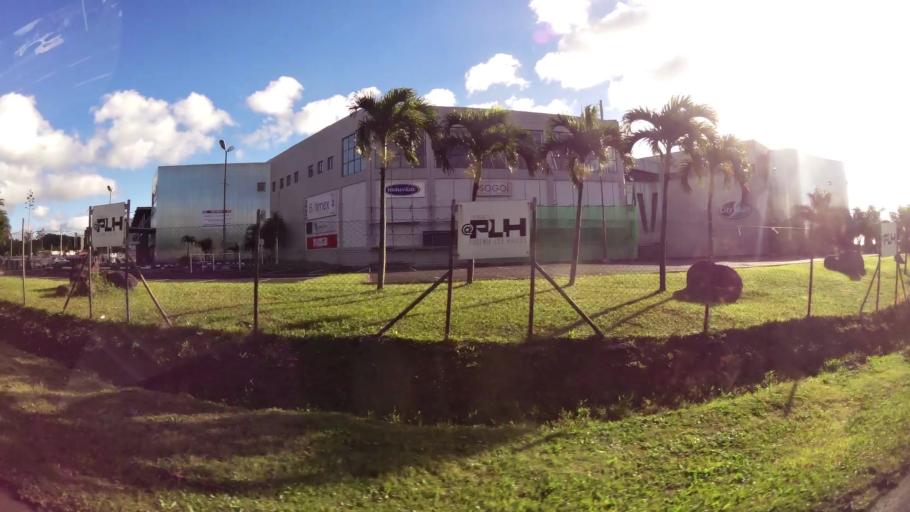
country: MU
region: Plaines Wilhems
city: Quatre Bornes
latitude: -20.2727
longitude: 57.4968
